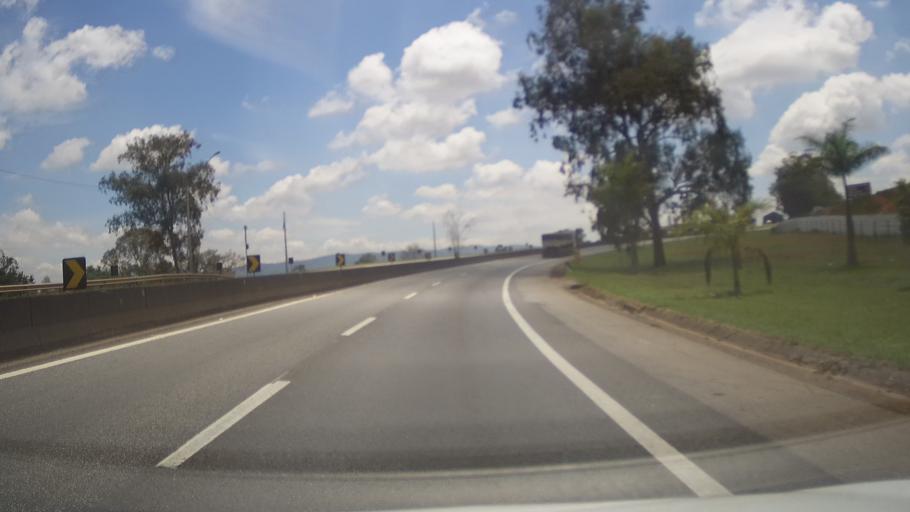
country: BR
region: Minas Gerais
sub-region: Sao Goncalo Do Sapucai
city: Sao Goncalo do Sapucai
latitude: -21.9511
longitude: -45.6244
